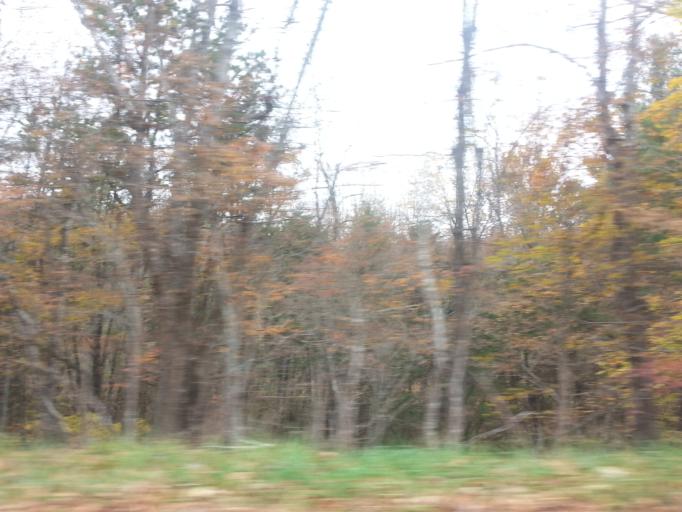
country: US
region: Virginia
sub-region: Pulaski County
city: Pulaski
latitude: 37.0880
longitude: -80.9273
